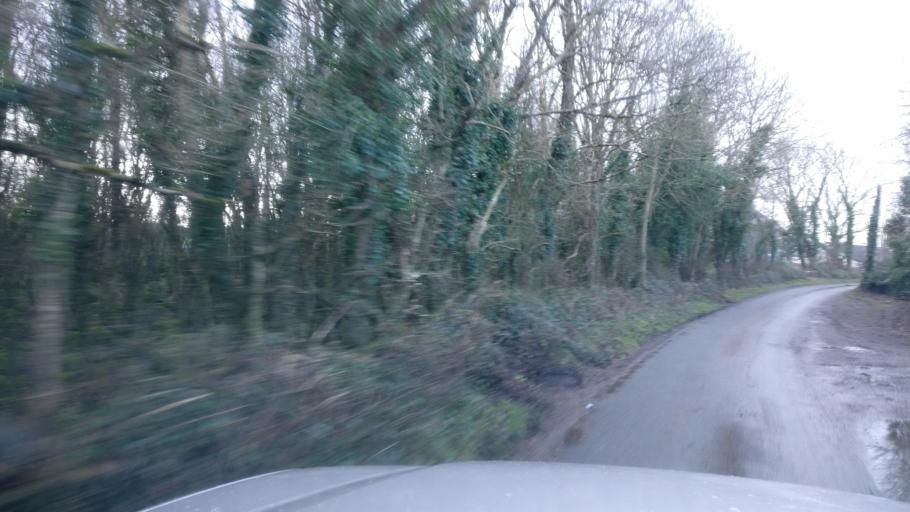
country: IE
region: Connaught
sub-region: County Galway
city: Oranmore
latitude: 53.2594
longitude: -8.8932
